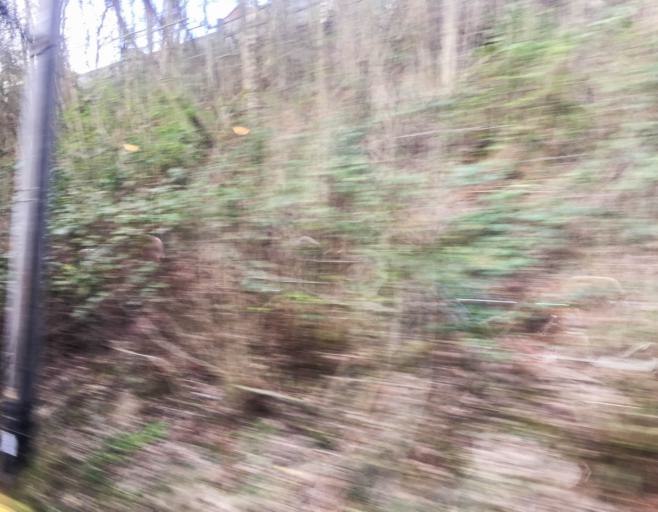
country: GB
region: Scotland
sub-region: West Dunbartonshire
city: Old Kilpatrick
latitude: 55.9208
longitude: -4.4474
